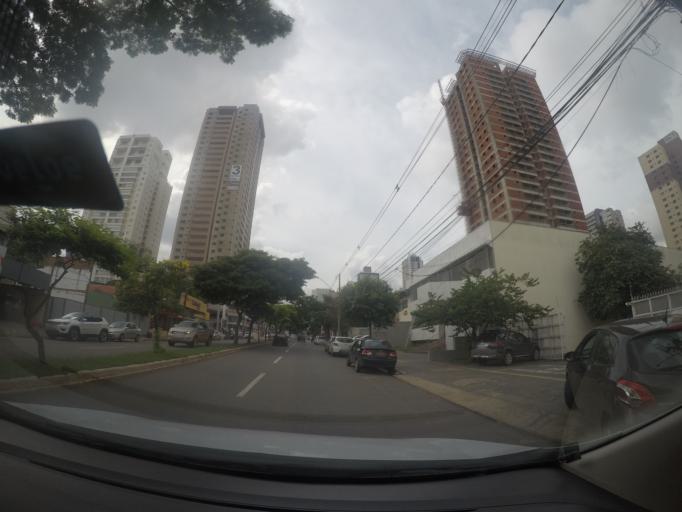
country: BR
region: Goias
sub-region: Goiania
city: Goiania
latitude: -16.6992
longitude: -49.2755
